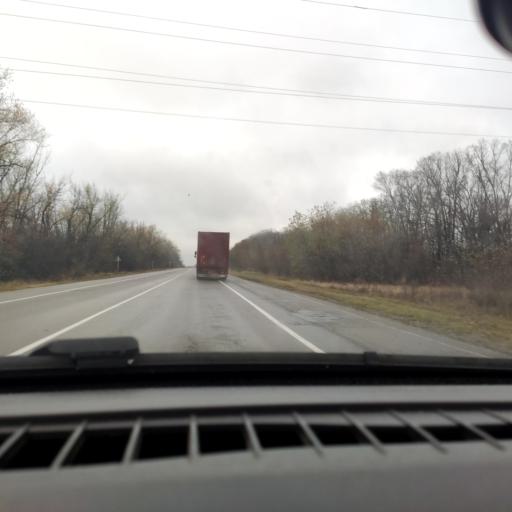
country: RU
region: Voronezj
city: Kolodeznyy
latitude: 51.2587
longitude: 39.0525
